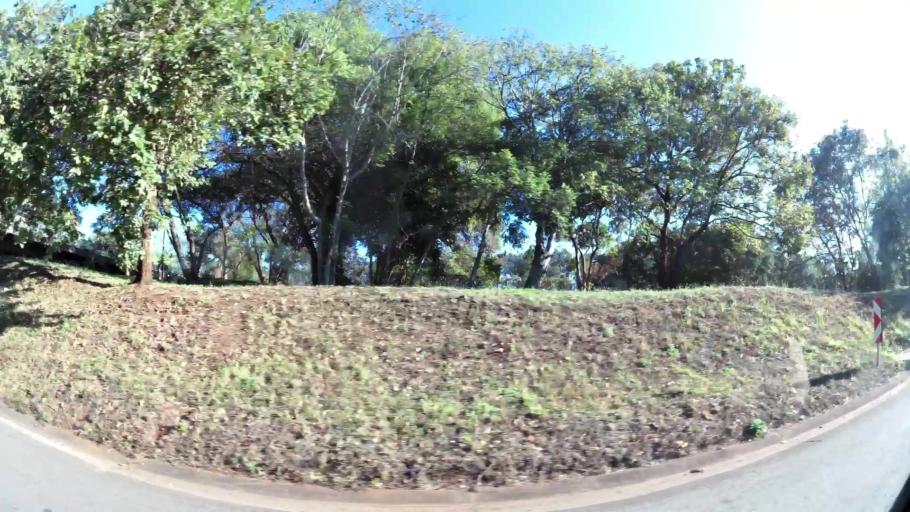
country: ZA
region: Limpopo
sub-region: Mopani District Municipality
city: Tzaneen
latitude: -23.8287
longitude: 30.1515
